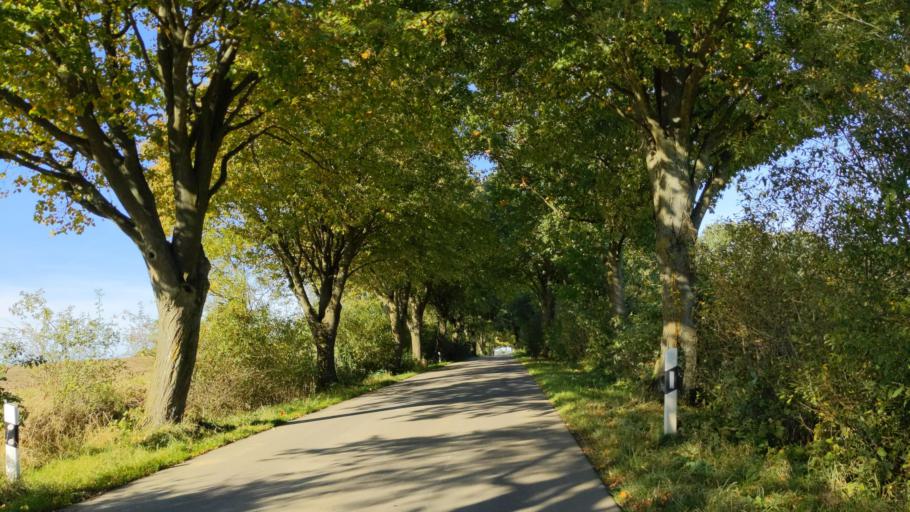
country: DE
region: Schleswig-Holstein
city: Ahrensbok
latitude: 54.0215
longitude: 10.6196
